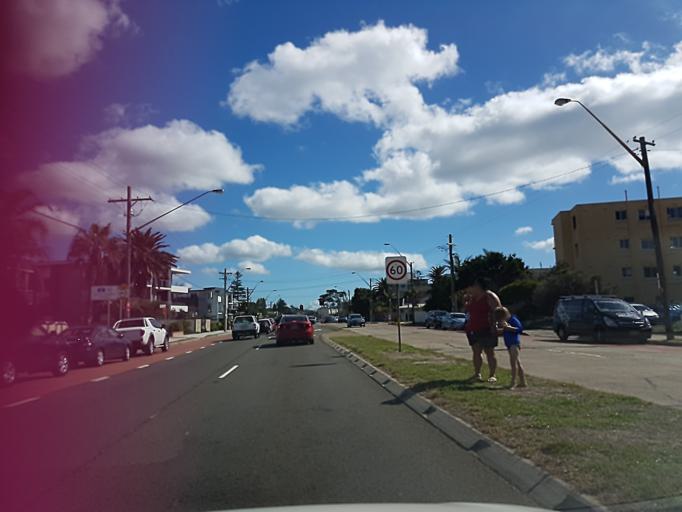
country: AU
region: New South Wales
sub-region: Warringah
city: Narrabeen
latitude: -33.7231
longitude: 151.2986
